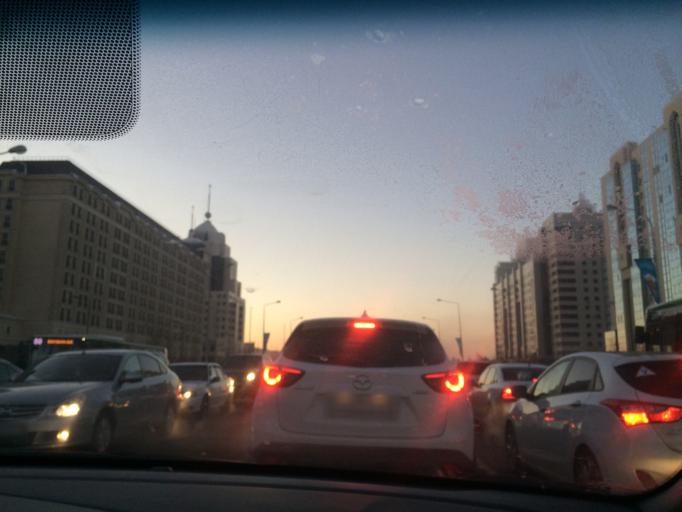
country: KZ
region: Astana Qalasy
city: Astana
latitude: 51.1624
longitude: 71.4100
